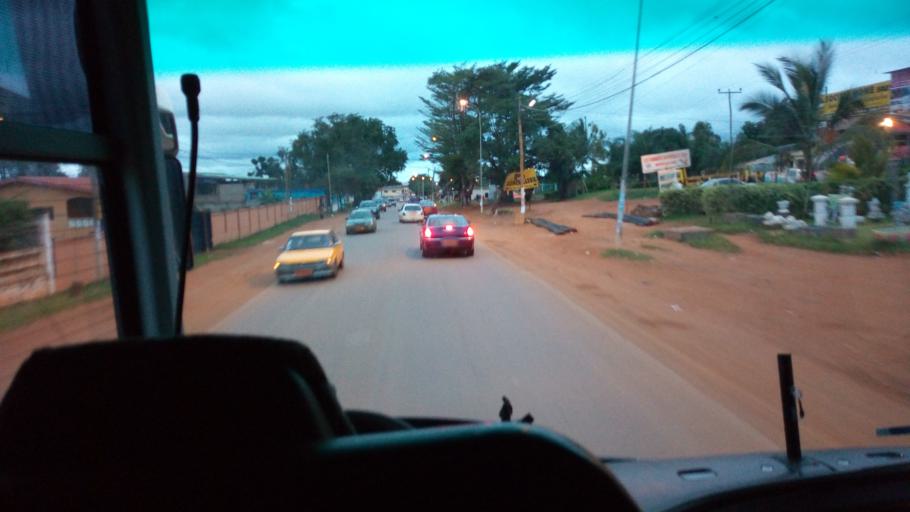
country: CM
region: Centre
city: Yaounde
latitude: 3.7913
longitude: 11.5228
